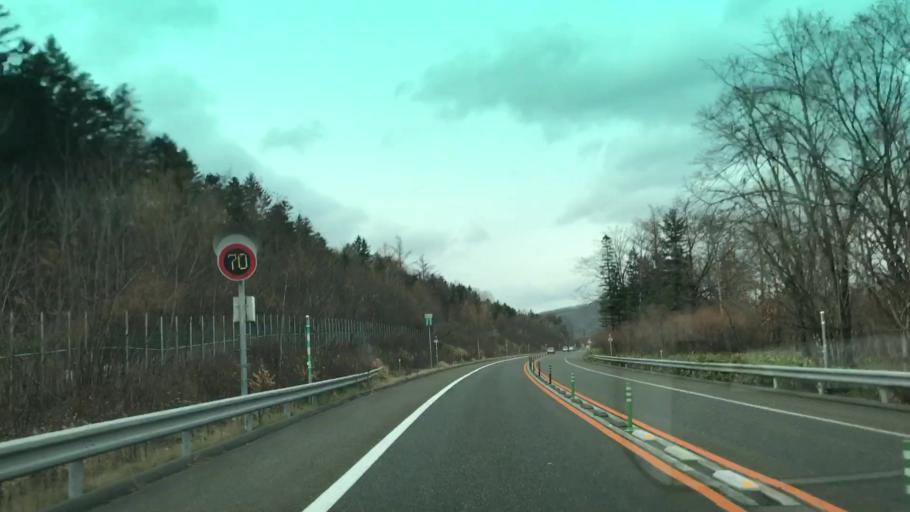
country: JP
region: Hokkaido
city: Otofuke
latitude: 43.0106
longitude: 142.8344
